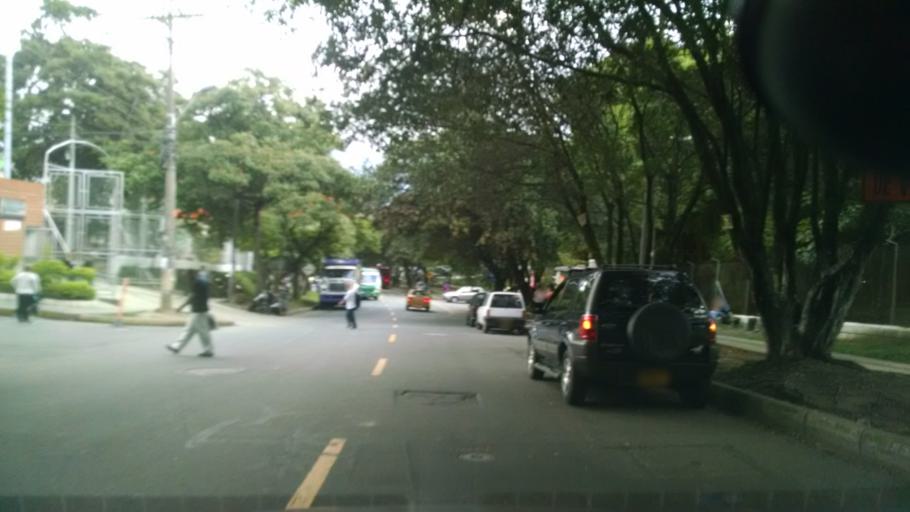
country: CO
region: Antioquia
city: Medellin
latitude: 6.2802
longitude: -75.5842
